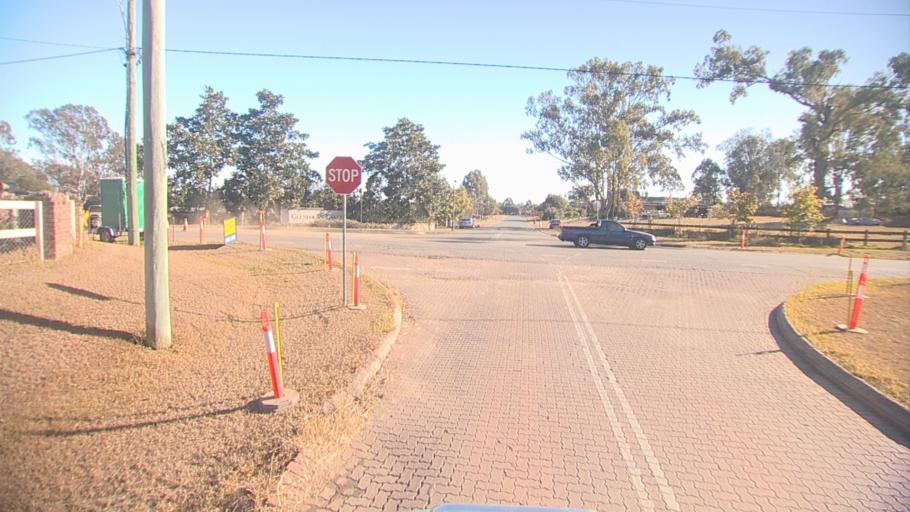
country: AU
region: Queensland
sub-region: Logan
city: Cedar Vale
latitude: -27.8322
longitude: 153.0052
